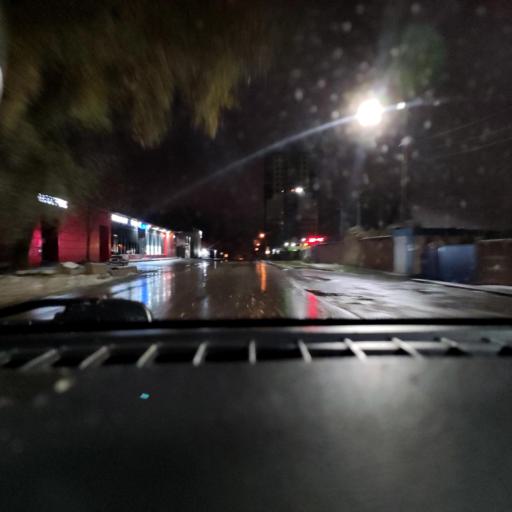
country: RU
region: Perm
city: Kondratovo
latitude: 57.9716
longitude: 56.1823
